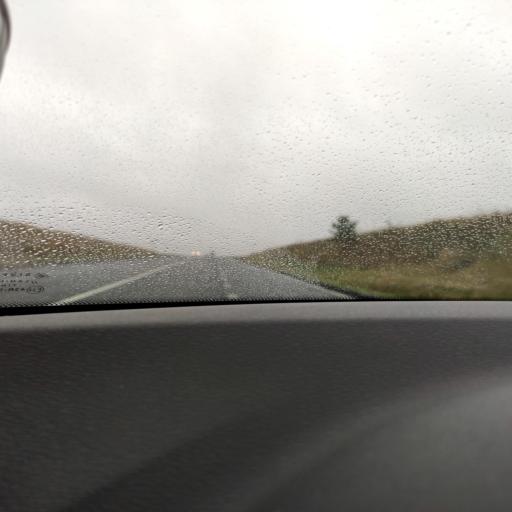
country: RU
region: Samara
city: Yelkhovka
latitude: 53.7322
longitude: 50.2309
